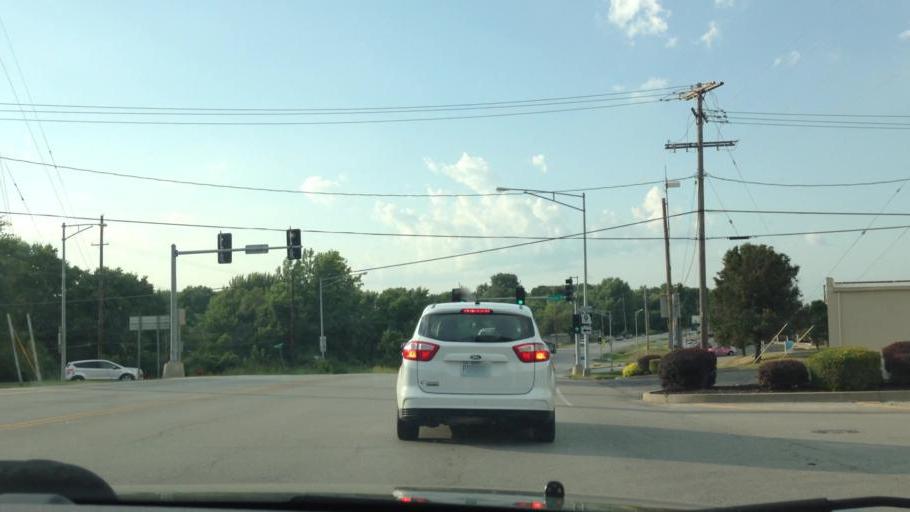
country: US
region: Missouri
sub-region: Platte County
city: Weatherby Lake
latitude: 39.2325
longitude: -94.6581
